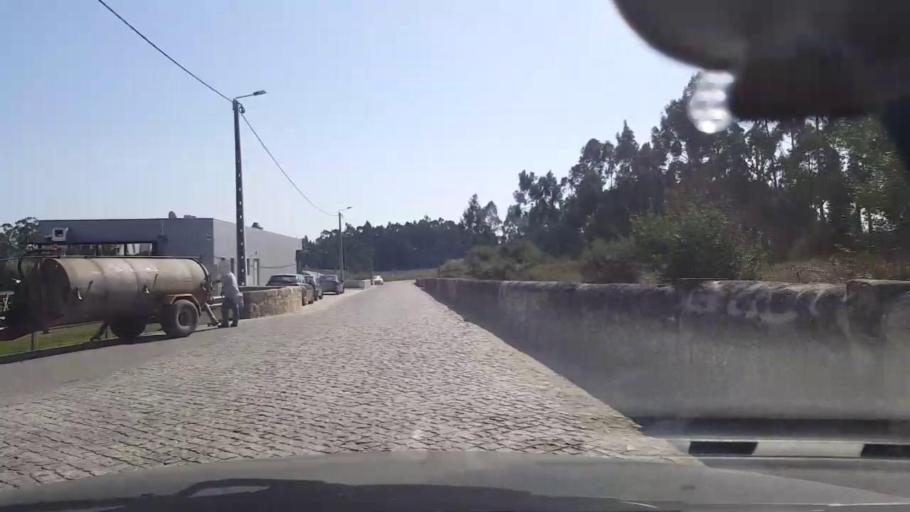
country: PT
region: Porto
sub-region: Vila do Conde
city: Vila do Conde
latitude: 41.3822
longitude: -8.7180
